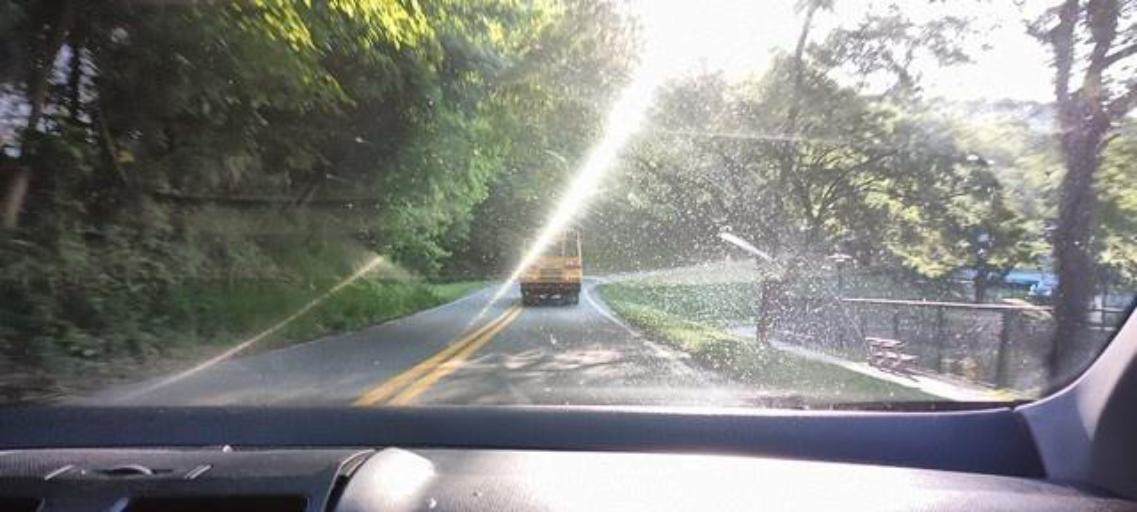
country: US
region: West Virginia
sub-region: Ohio County
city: Bethlehem
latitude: 40.0606
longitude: -80.6667
